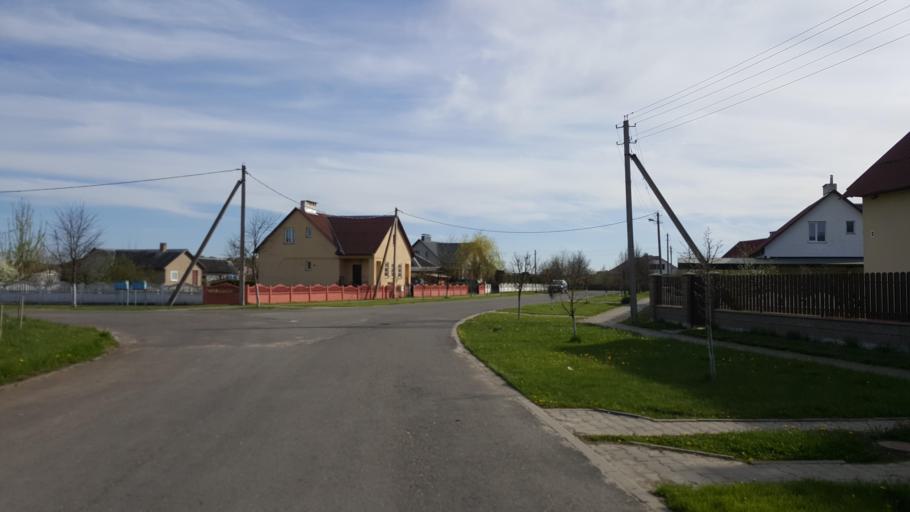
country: BY
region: Brest
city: Vysokaye
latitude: 52.4074
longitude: 23.4619
